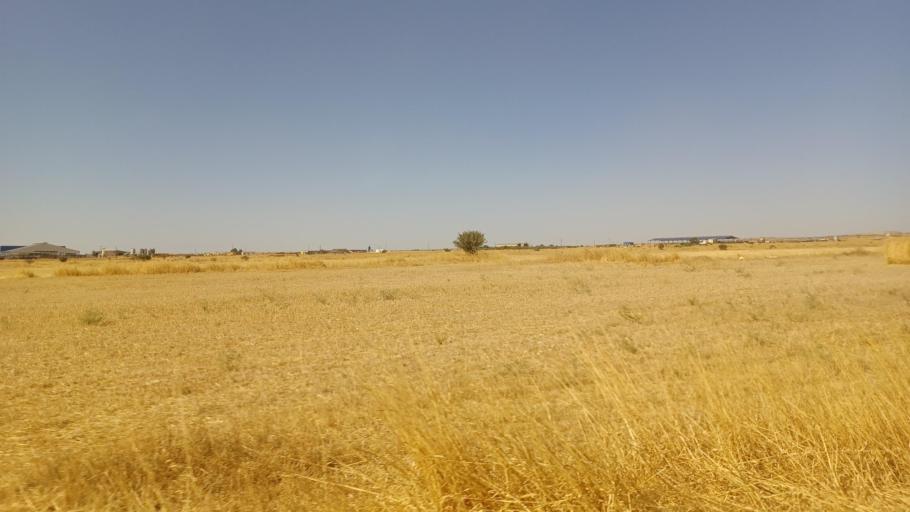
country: CY
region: Larnaka
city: Pergamos
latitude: 35.0392
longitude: 33.6903
